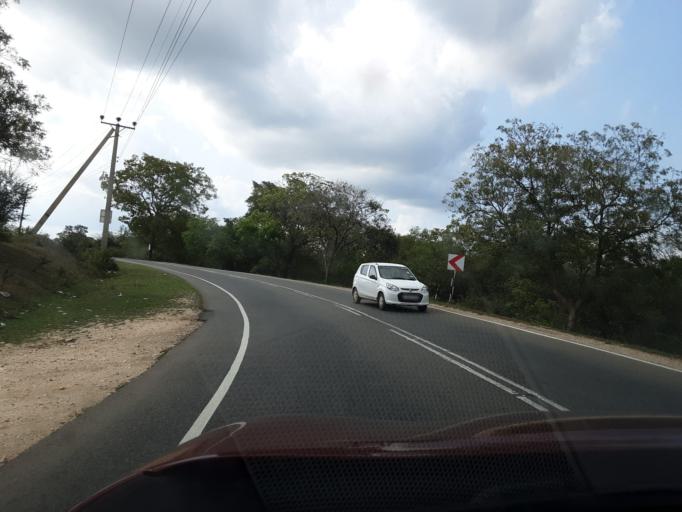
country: LK
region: Uva
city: Haputale
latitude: 6.5083
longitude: 81.1307
